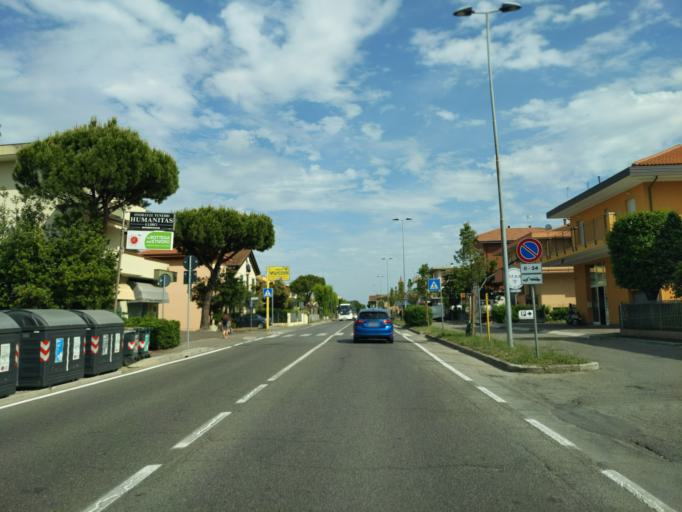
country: IT
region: Emilia-Romagna
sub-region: Provincia di Rimini
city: Rimini
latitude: 44.0448
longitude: 12.5853
